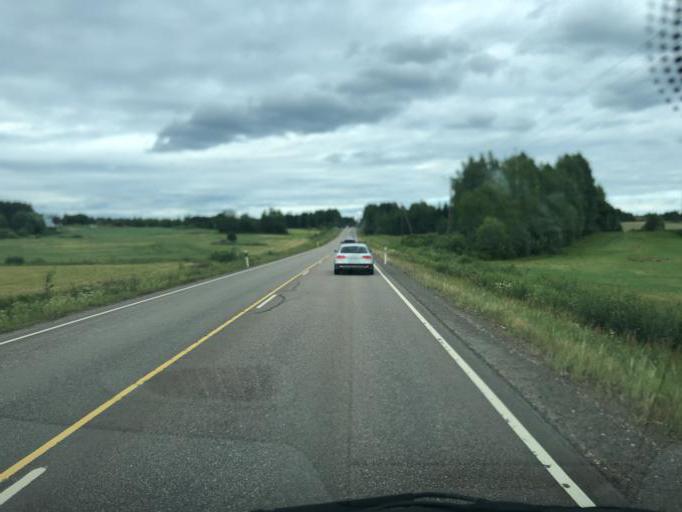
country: FI
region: Southern Savonia
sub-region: Mikkeli
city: Maentyharju
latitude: 61.0828
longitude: 27.0636
